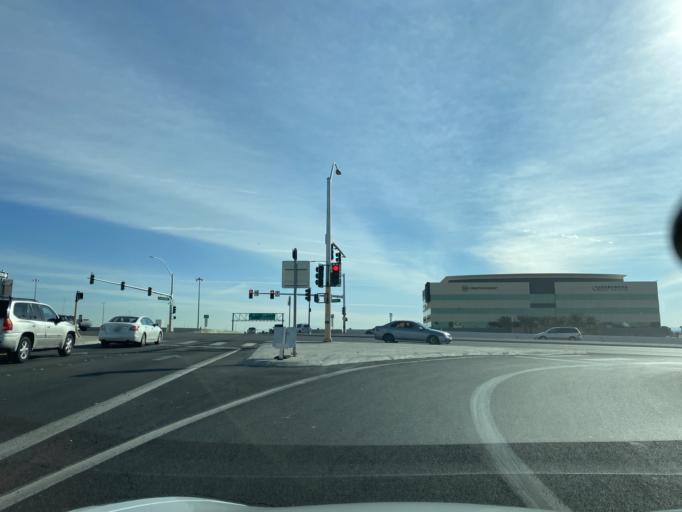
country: US
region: Nevada
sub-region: Clark County
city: Las Vegas
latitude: 36.2636
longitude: -115.2551
